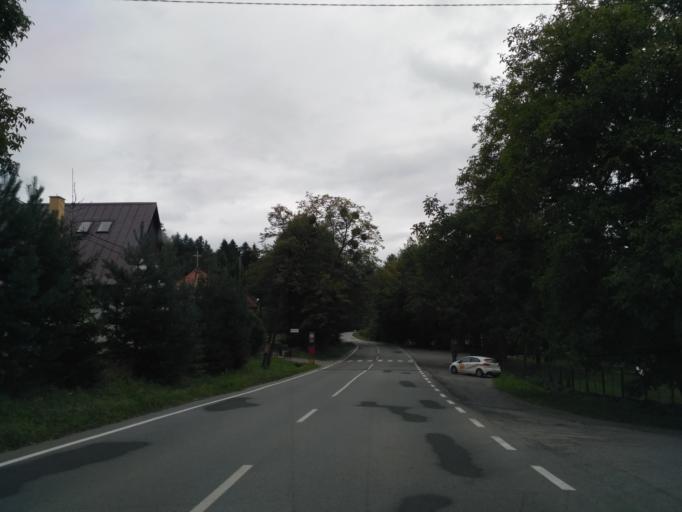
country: SK
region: Presovsky
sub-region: Okres Presov
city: Presov
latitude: 48.9843
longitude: 21.1753
